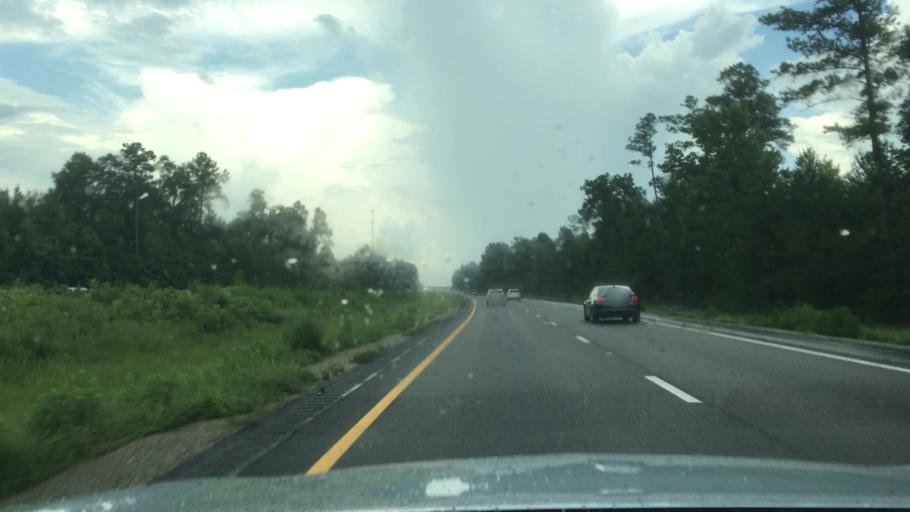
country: US
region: Mississippi
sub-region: Lamar County
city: Purvis
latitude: 31.1779
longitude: -89.3470
